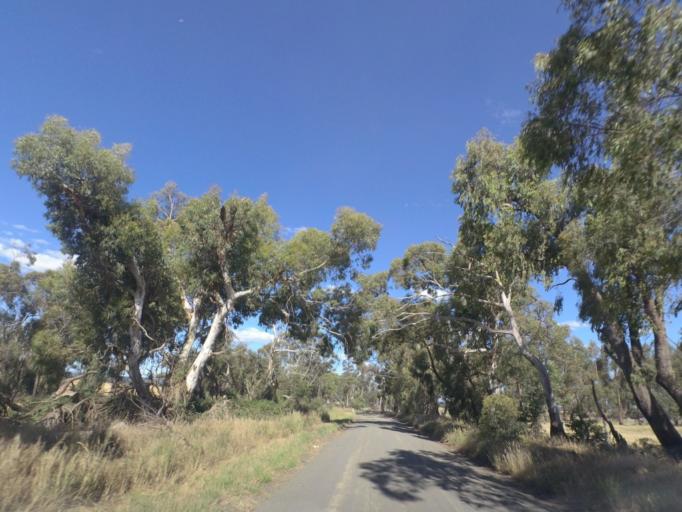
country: AU
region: Victoria
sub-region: Hume
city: Craigieburn
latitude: -37.4265
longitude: 144.9563
